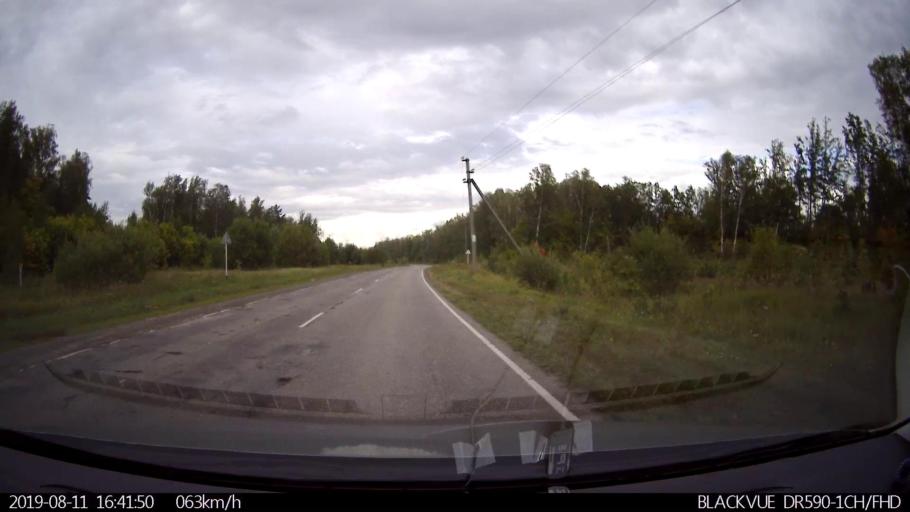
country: RU
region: Ulyanovsk
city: Mayna
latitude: 54.1560
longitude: 47.6566
